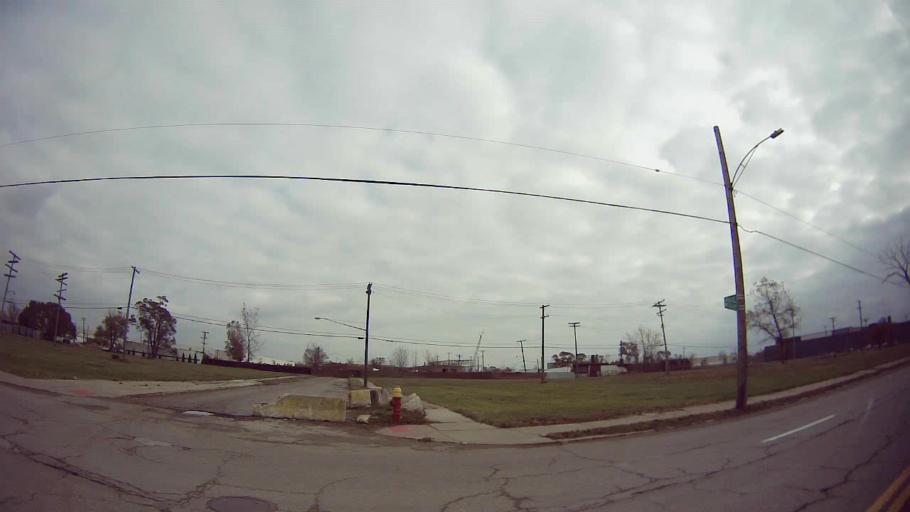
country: US
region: Michigan
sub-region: Wayne County
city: Hamtramck
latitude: 42.3950
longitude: -83.0375
